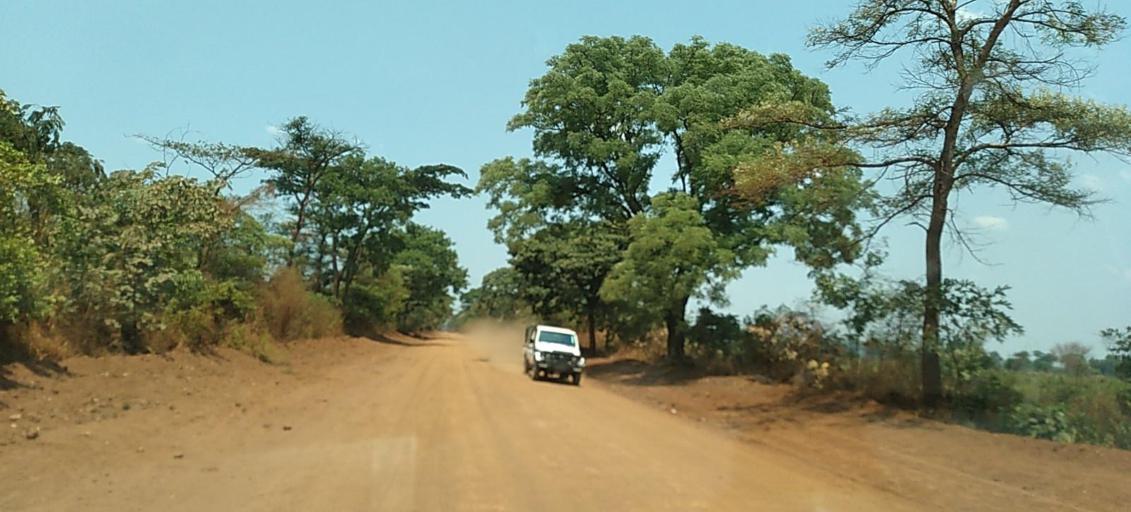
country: ZM
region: Copperbelt
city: Mpongwe
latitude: -13.5151
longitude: 28.0155
